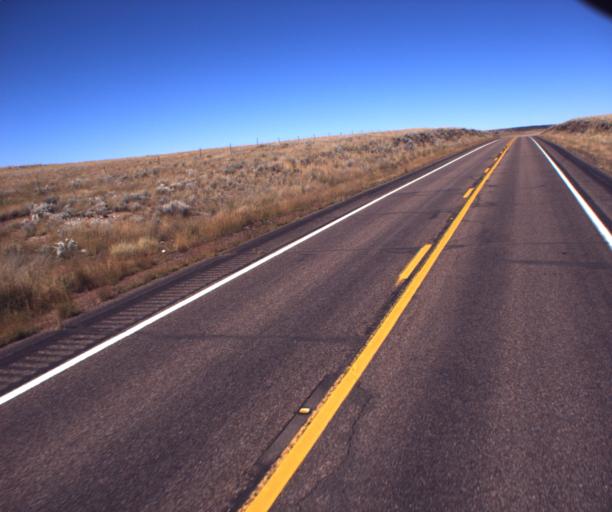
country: US
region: Arizona
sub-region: Apache County
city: Saint Johns
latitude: 34.3096
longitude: -109.3795
